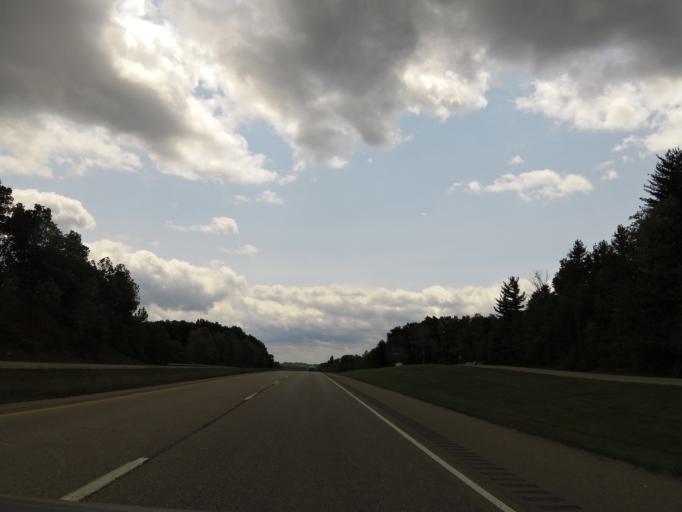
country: US
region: Ohio
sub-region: Meigs County
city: Pomeroy
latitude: 39.1279
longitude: -82.0193
